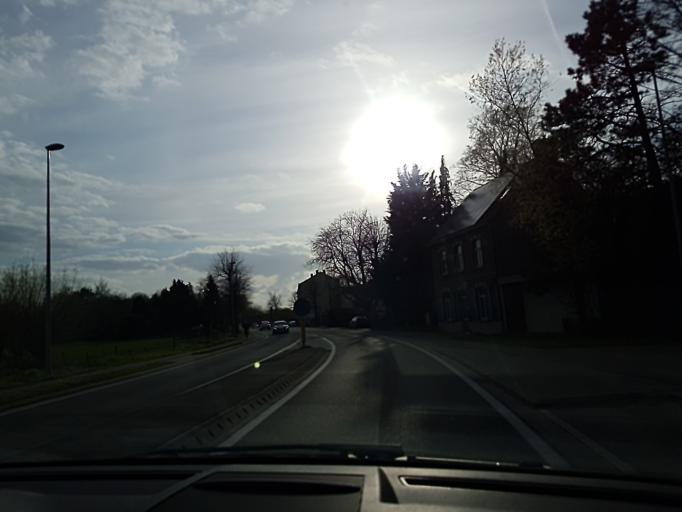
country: BE
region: Flanders
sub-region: Provincie West-Vlaanderen
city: Oostkamp
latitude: 51.1551
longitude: 3.1853
